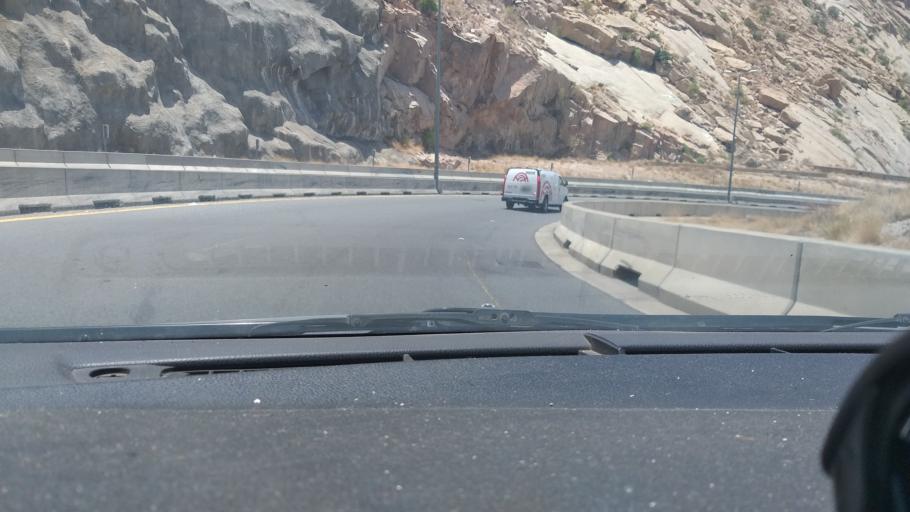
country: SA
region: Makkah
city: Al Hada
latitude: 21.3377
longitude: 40.2580
